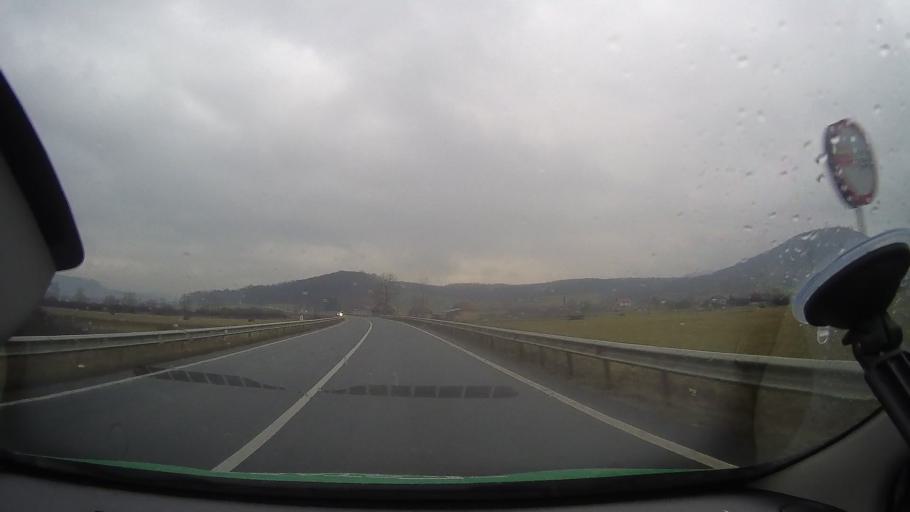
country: RO
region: Hunedoara
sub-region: Comuna Baia de Cris
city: Baia de Cris
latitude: 46.1784
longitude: 22.6852
